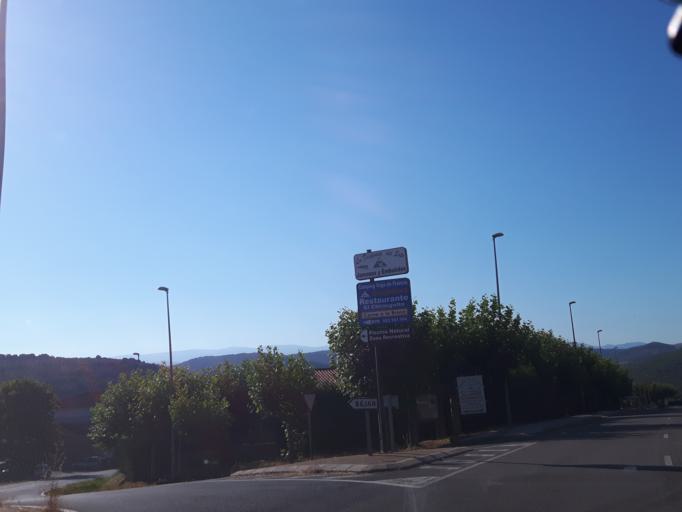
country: ES
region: Castille and Leon
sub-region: Provincia de Salamanca
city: Sotoserrano
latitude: 40.4347
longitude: -6.0319
